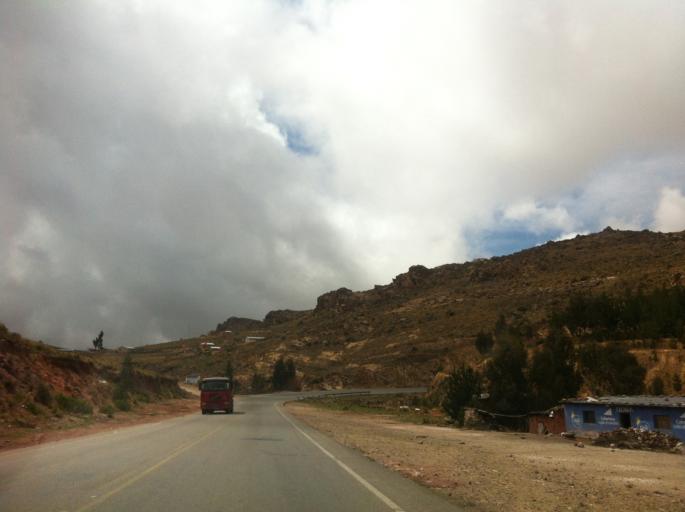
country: BO
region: Cochabamba
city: Irpa Irpa
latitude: -17.7010
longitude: -66.4783
